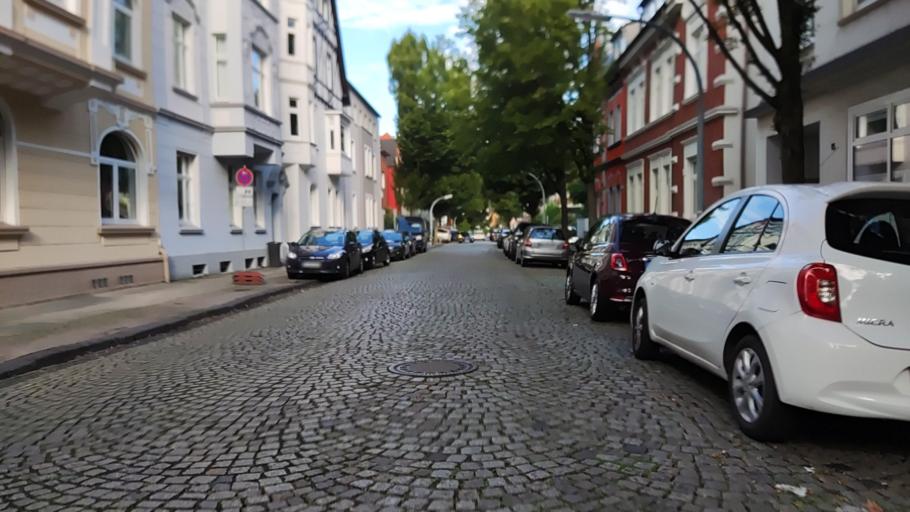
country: DE
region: North Rhine-Westphalia
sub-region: Regierungsbezirk Arnsberg
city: Herne
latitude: 51.5327
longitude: 7.2270
